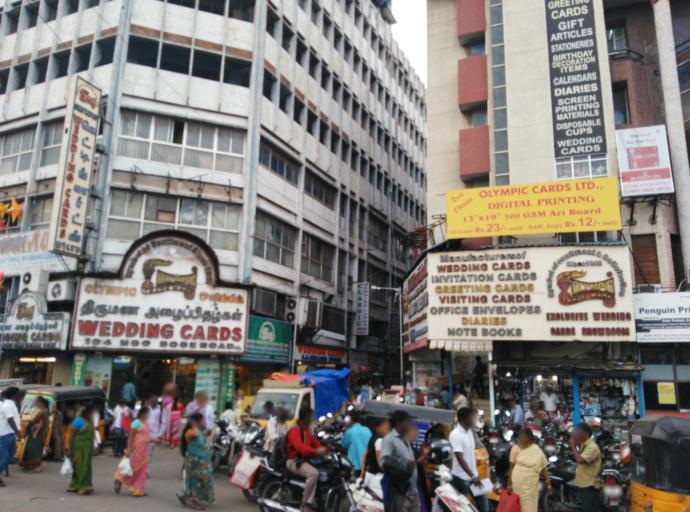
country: IN
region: Tamil Nadu
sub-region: Chennai
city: Chennai
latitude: 13.0884
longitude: 80.2837
